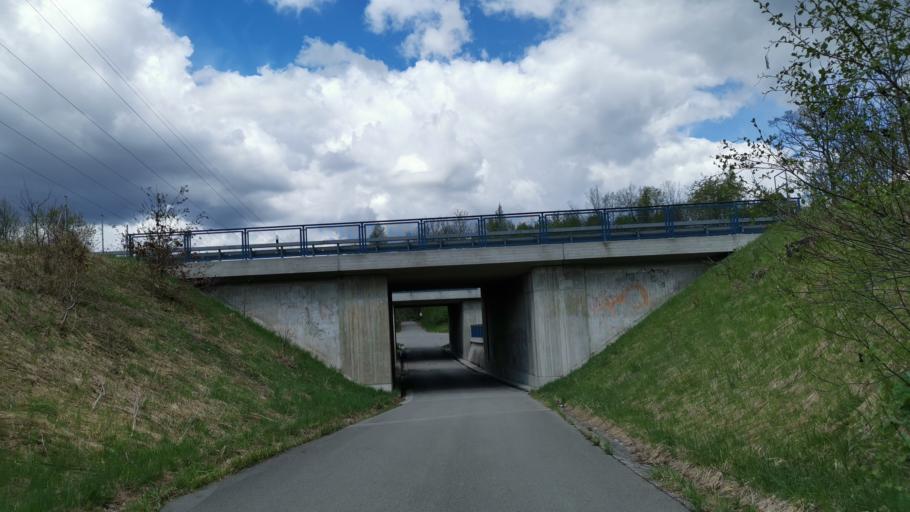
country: DE
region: Bavaria
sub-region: Upper Bavaria
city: Neuried
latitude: 48.0538
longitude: 11.4598
